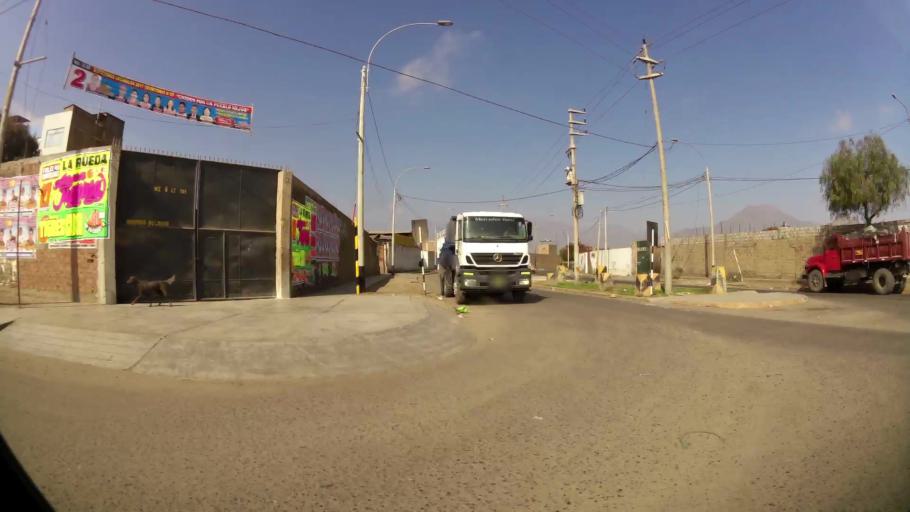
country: PE
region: La Libertad
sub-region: Provincia de Trujillo
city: Trujillo
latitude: -8.1118
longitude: -79.0029
